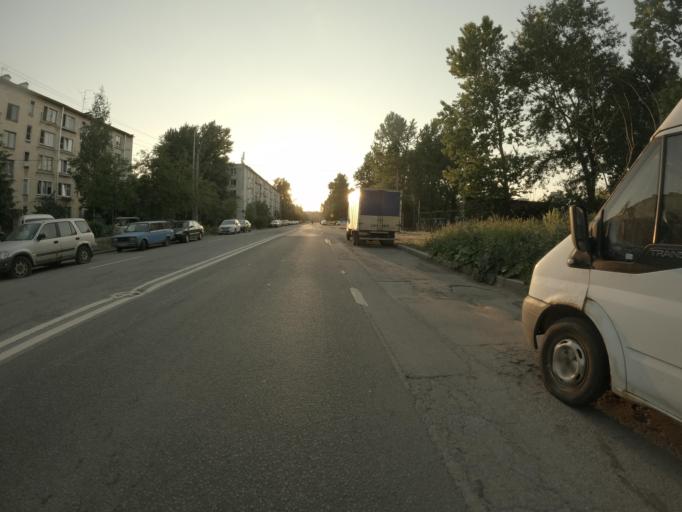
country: RU
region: St.-Petersburg
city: Avtovo
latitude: 59.8679
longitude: 30.2793
